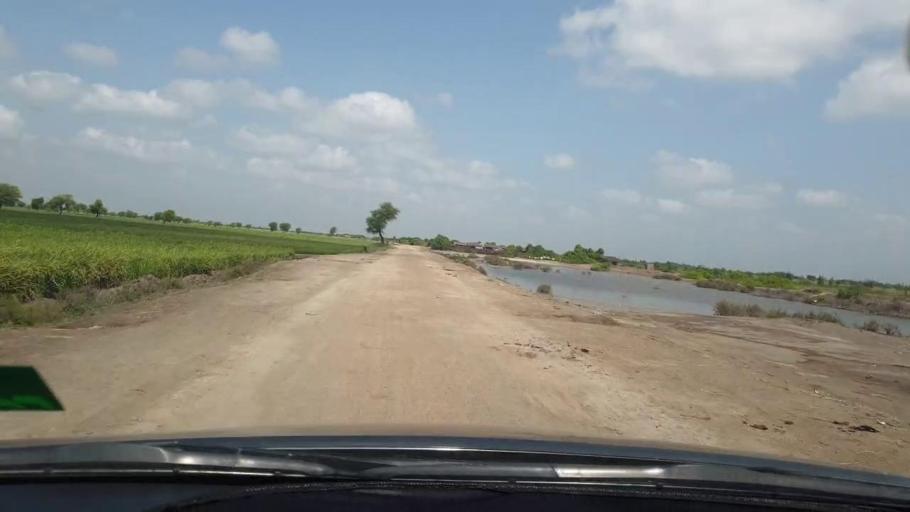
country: PK
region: Sindh
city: Tando Bago
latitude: 24.8577
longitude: 69.0585
